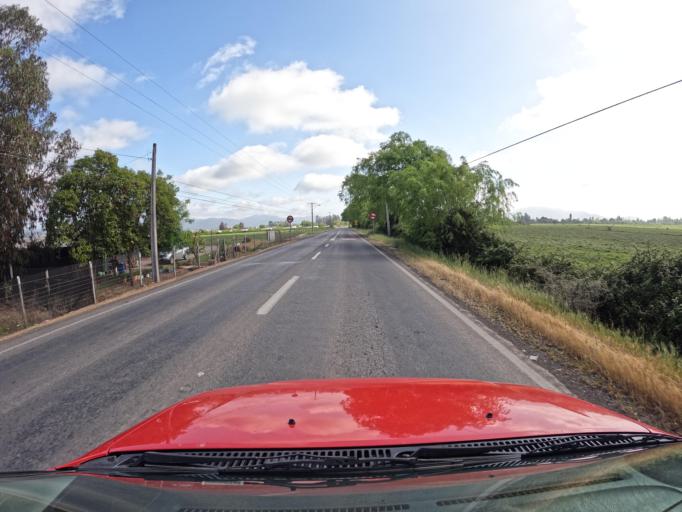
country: CL
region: Maule
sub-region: Provincia de Curico
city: Rauco
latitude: -34.8930
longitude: -71.2739
